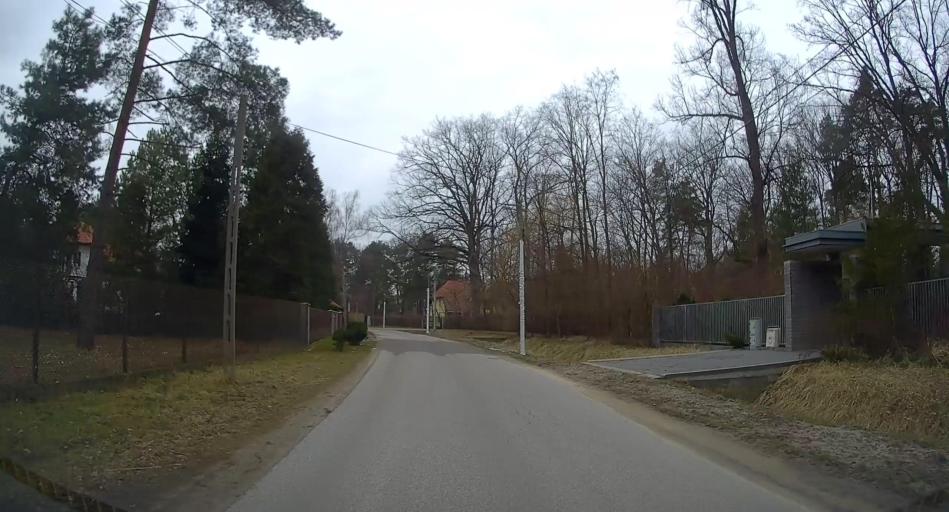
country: PL
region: Masovian Voivodeship
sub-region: Powiat piaseczynski
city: Piaseczno
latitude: 52.0628
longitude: 20.9993
